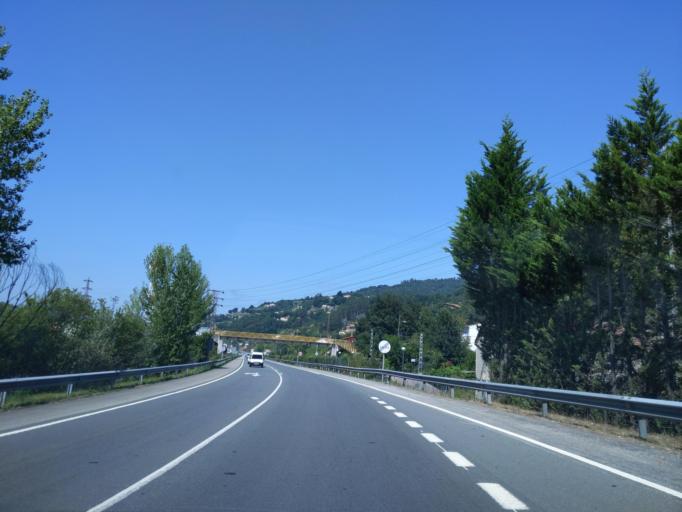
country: ES
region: Asturias
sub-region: Province of Asturias
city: El entrego
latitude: 43.2873
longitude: -5.6253
